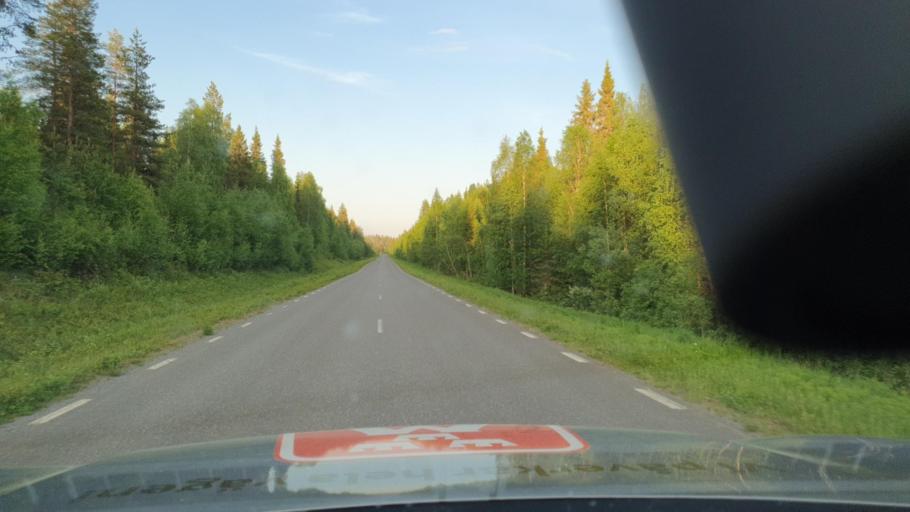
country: SE
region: Norrbotten
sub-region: Bodens Kommun
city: Boden
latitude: 66.2058
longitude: 21.4611
